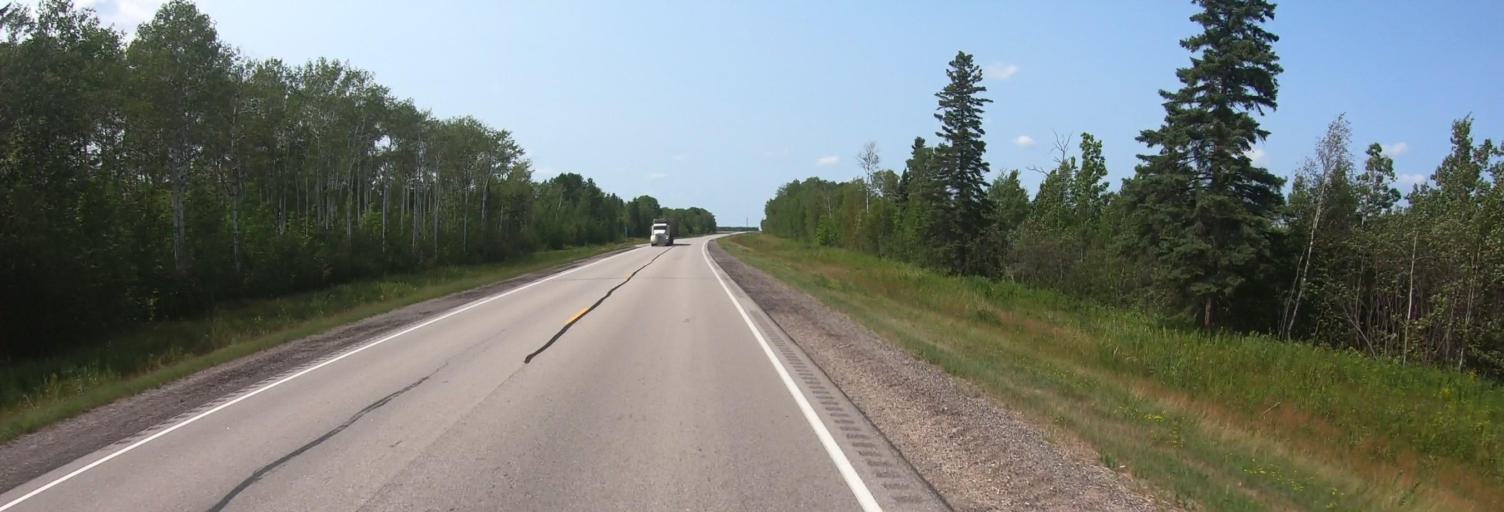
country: US
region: Minnesota
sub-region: Lake of the Woods County
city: Baudette
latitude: 48.7151
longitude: -94.7299
